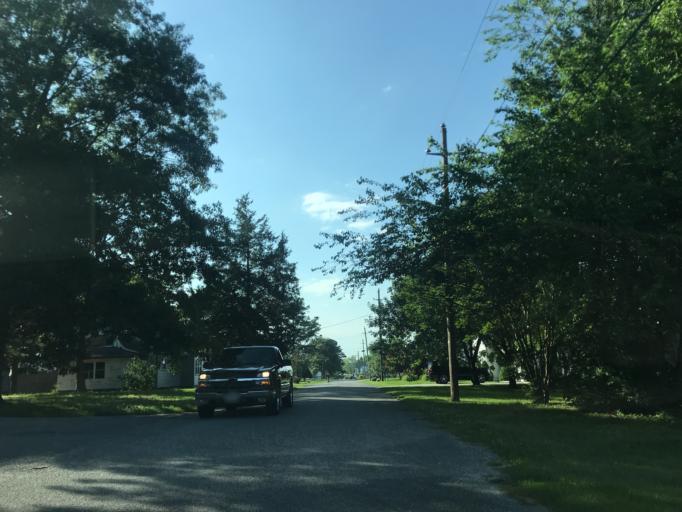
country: US
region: Maryland
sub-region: Wicomico County
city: Hebron
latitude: 38.5409
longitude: -75.7157
